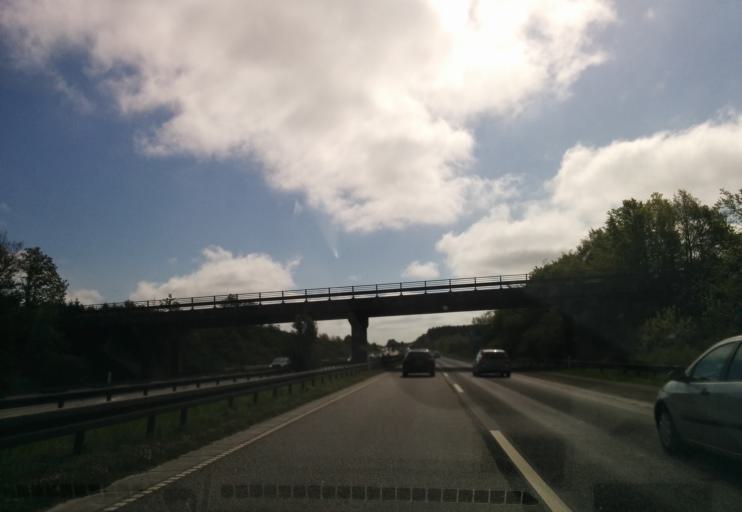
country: DK
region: South Denmark
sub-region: Assens Kommune
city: Vissenbjerg
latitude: 55.4015
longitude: 10.1546
